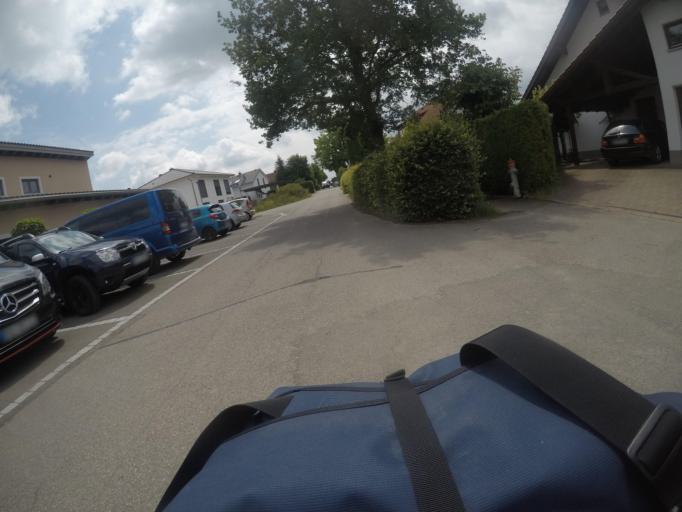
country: DE
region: Bavaria
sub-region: Swabia
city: Fellheim
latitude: 48.0759
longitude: 10.1562
